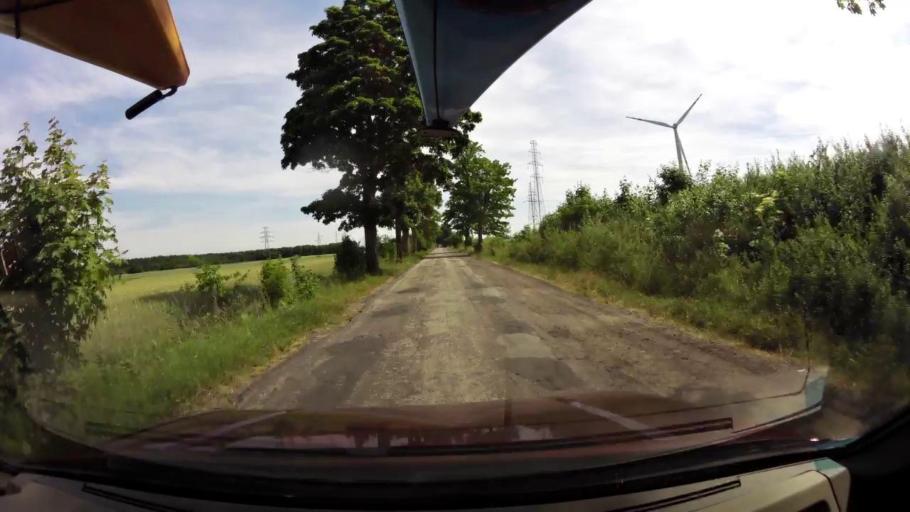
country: PL
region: West Pomeranian Voivodeship
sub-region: Powiat koszalinski
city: Sianow
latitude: 54.3188
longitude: 16.3235
